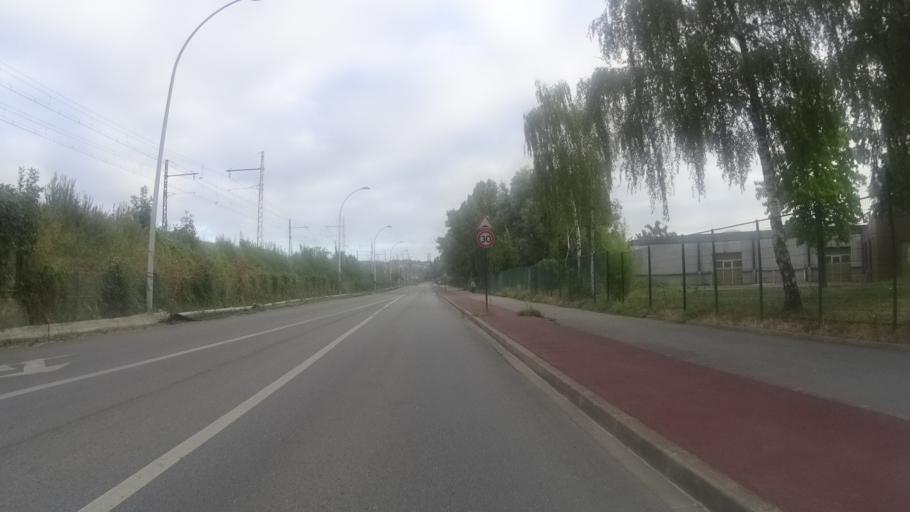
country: FR
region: Ile-de-France
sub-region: Departement de l'Essonne
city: Villabe
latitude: 48.5967
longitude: 2.4599
